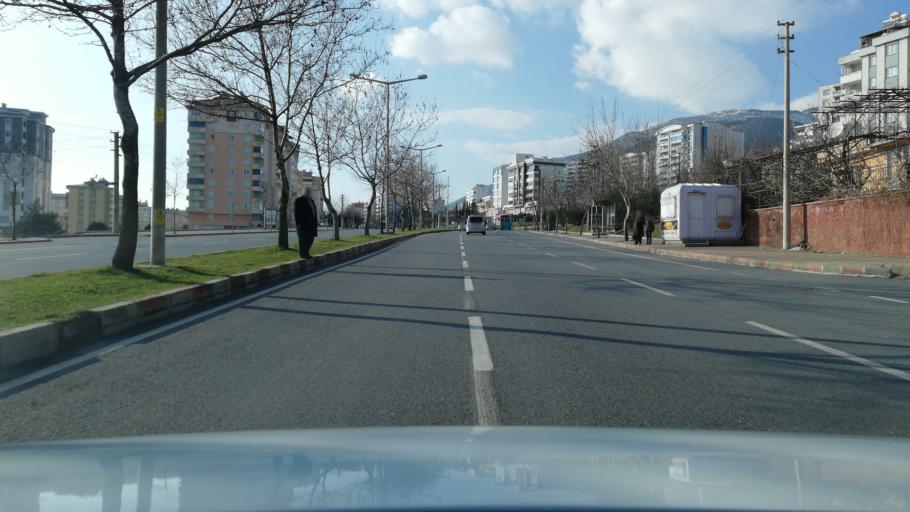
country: TR
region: Kahramanmaras
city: Kahramanmaras
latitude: 37.5947
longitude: 36.8928
